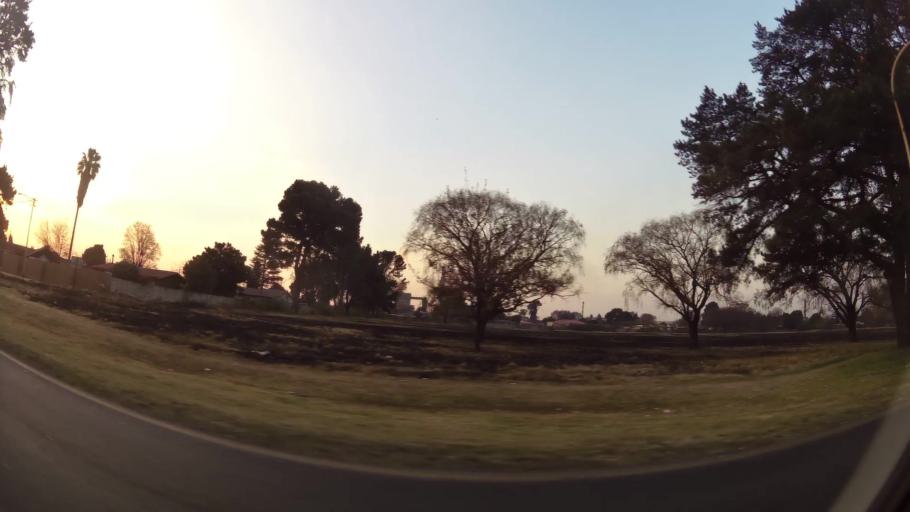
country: ZA
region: Gauteng
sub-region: Ekurhuleni Metropolitan Municipality
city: Springs
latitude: -26.2677
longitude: 28.4105
